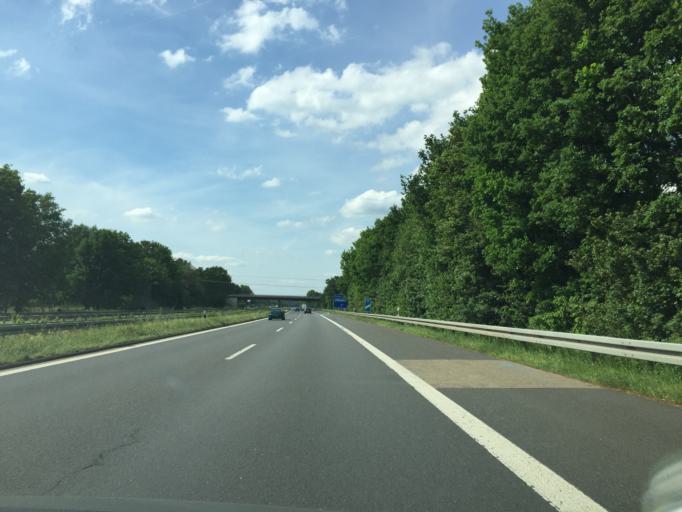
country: DE
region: Bavaria
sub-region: Regierungsbezirk Unterfranken
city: Alzenau in Unterfranken
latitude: 50.0442
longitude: 9.0556
